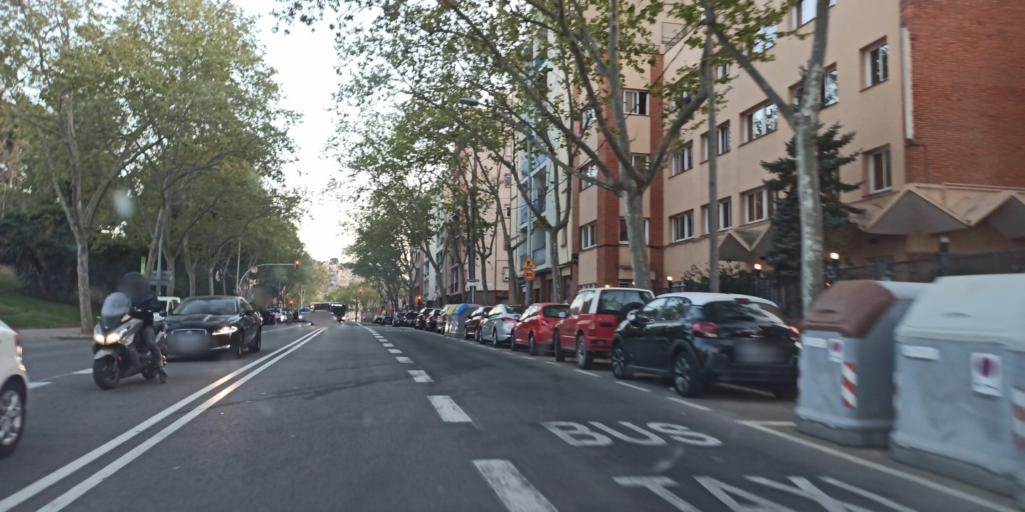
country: ES
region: Catalonia
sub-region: Provincia de Barcelona
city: Nou Barris
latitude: 41.4344
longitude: 2.1636
